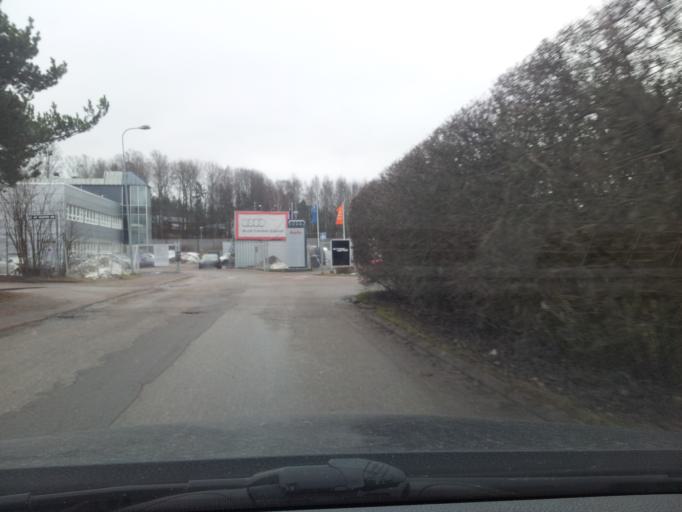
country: FI
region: Uusimaa
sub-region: Helsinki
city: Kauniainen
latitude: 60.1609
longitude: 24.6988
